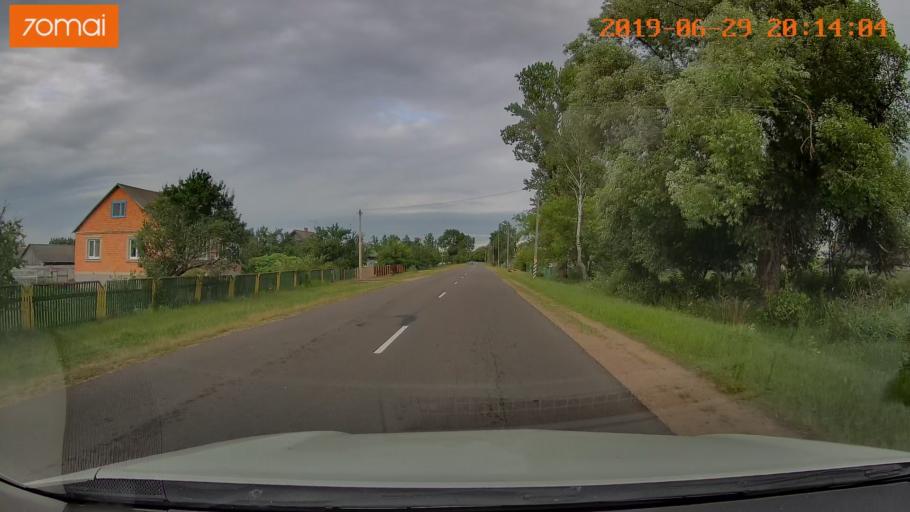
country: BY
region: Brest
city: Lahishyn
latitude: 52.3668
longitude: 26.1525
